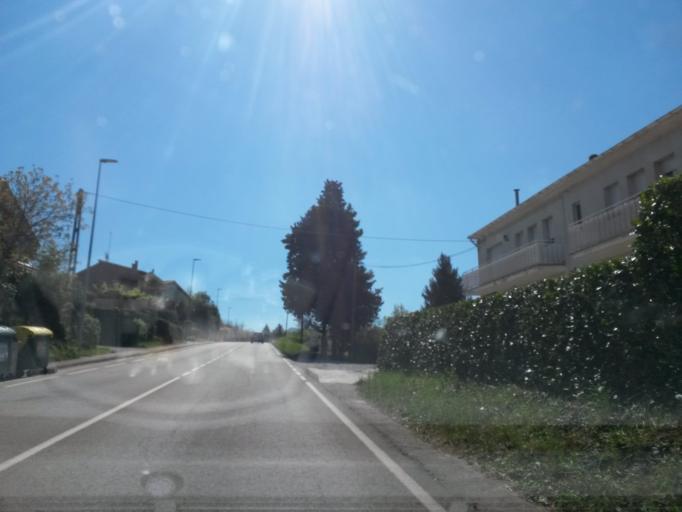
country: ES
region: Catalonia
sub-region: Provincia de Girona
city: Sant Cristofol de les Fonts
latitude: 42.1741
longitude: 2.4943
